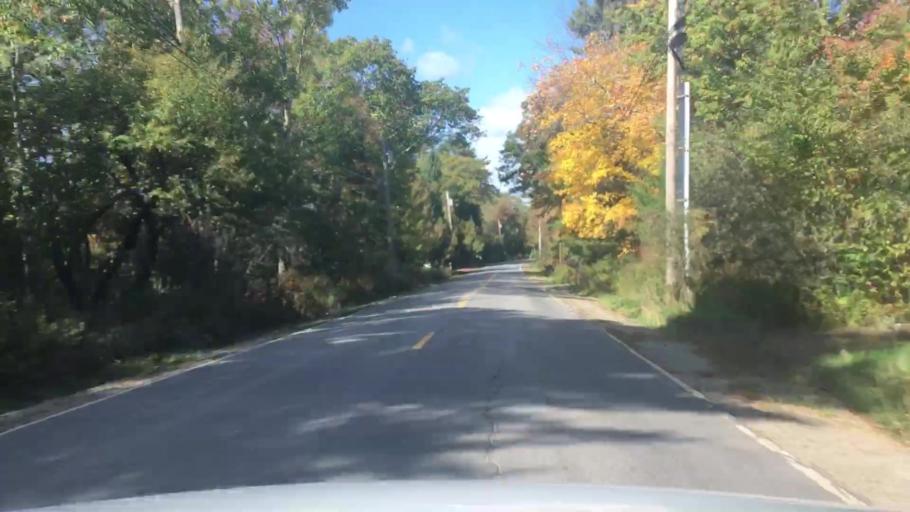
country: US
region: Maine
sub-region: Knox County
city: Warren
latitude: 44.0997
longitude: -69.2203
